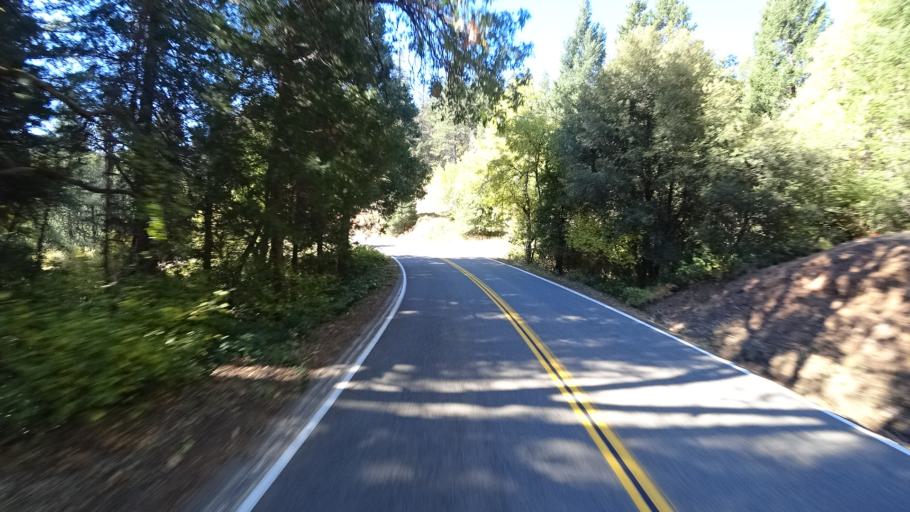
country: US
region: California
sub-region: Trinity County
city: Weaverville
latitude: 41.1952
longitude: -123.0728
